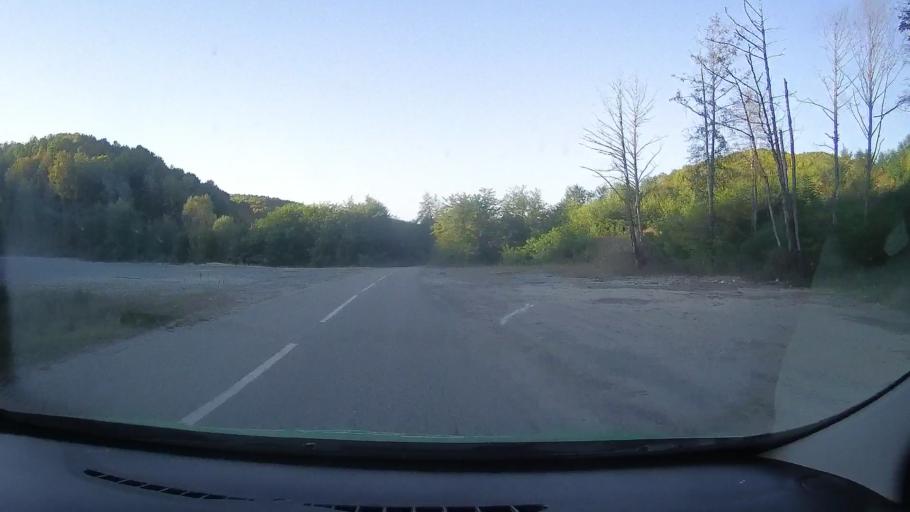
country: RO
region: Timis
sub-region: Comuna Fardea
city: Fardea
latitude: 45.6945
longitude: 22.1601
